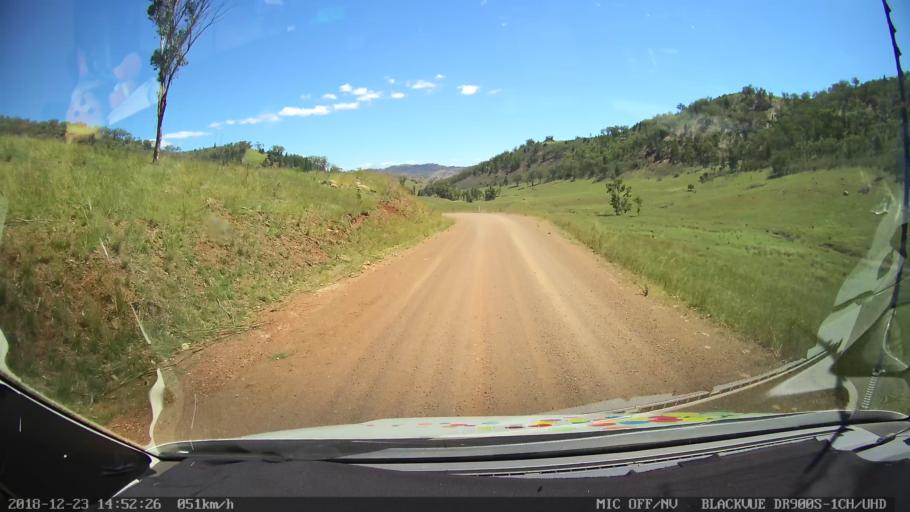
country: AU
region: New South Wales
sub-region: Tamworth Municipality
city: Manilla
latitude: -30.6842
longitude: 150.8543
